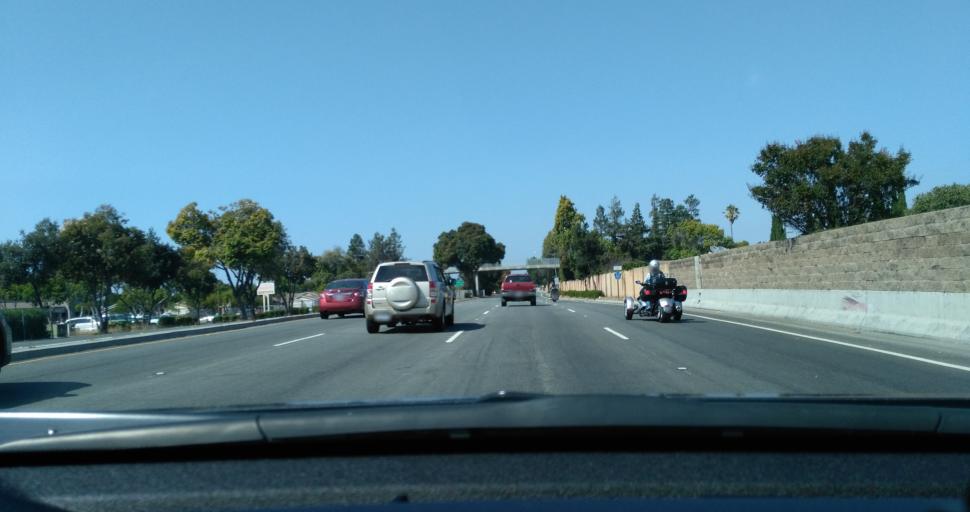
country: US
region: California
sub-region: Santa Clara County
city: Sunnyvale
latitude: 37.3963
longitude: -121.9956
